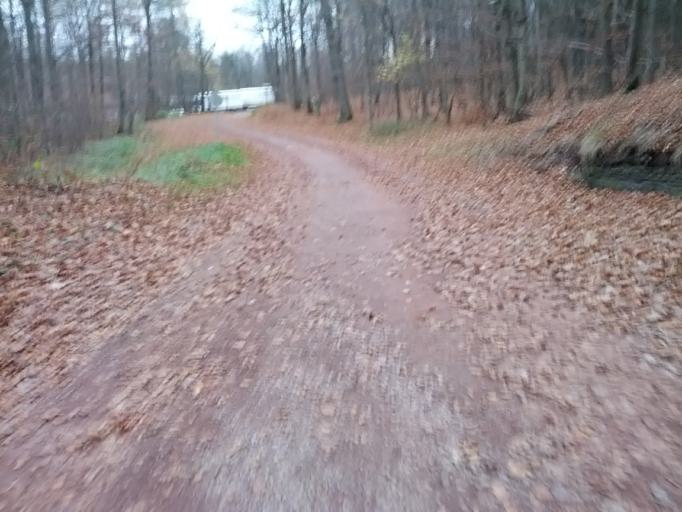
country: DE
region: Thuringia
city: Eisenach
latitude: 50.9309
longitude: 10.3199
